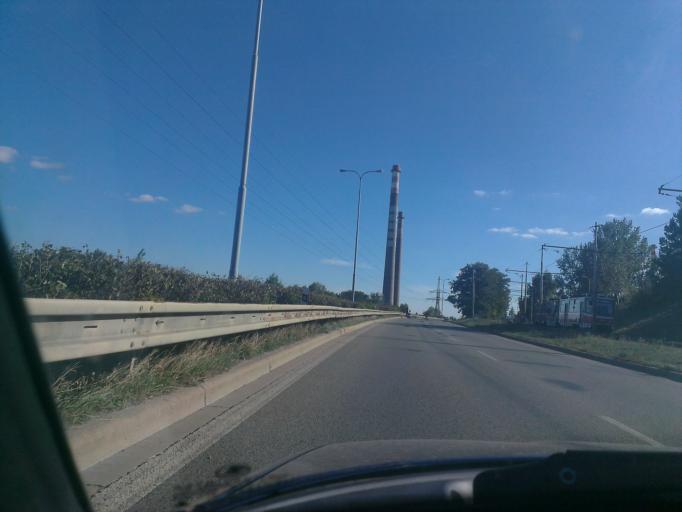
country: CZ
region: South Moravian
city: Bilovice nad Svitavou
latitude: 49.1959
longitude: 16.6670
